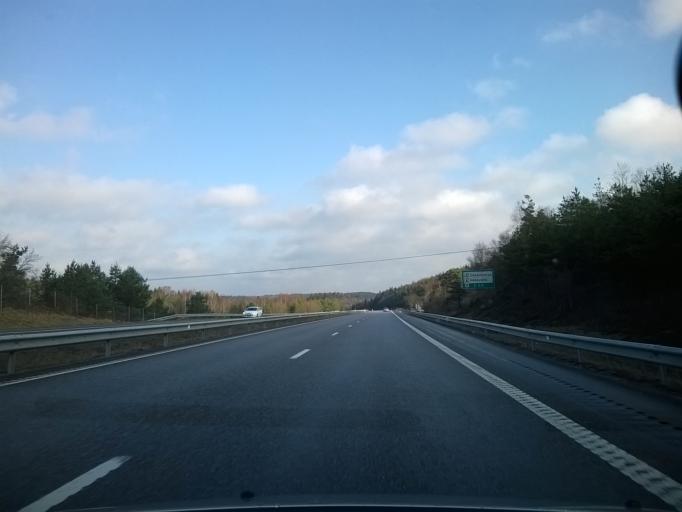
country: SE
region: Vaestra Goetaland
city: Svanesund
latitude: 58.0946
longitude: 11.8823
